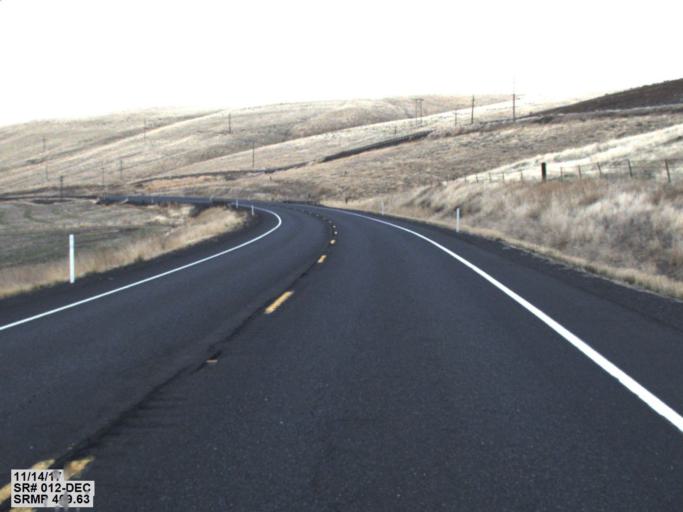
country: US
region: Washington
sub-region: Garfield County
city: Pomeroy
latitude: 46.4637
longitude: -117.4755
